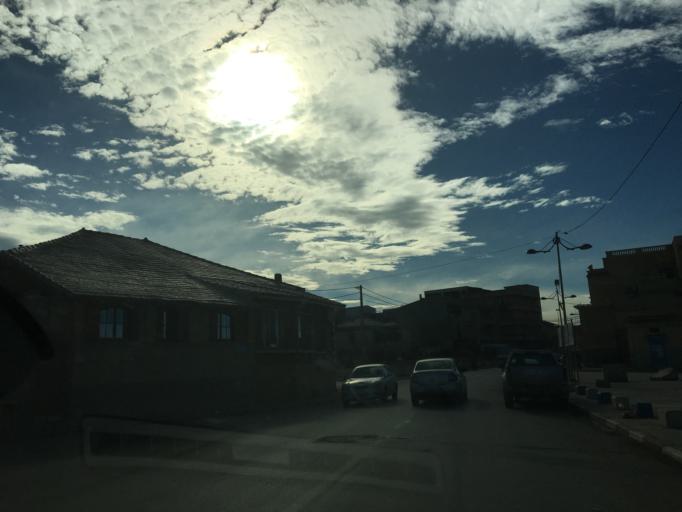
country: DZ
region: Alger
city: Bordj el Kiffan
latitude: 36.7461
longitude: 3.1804
